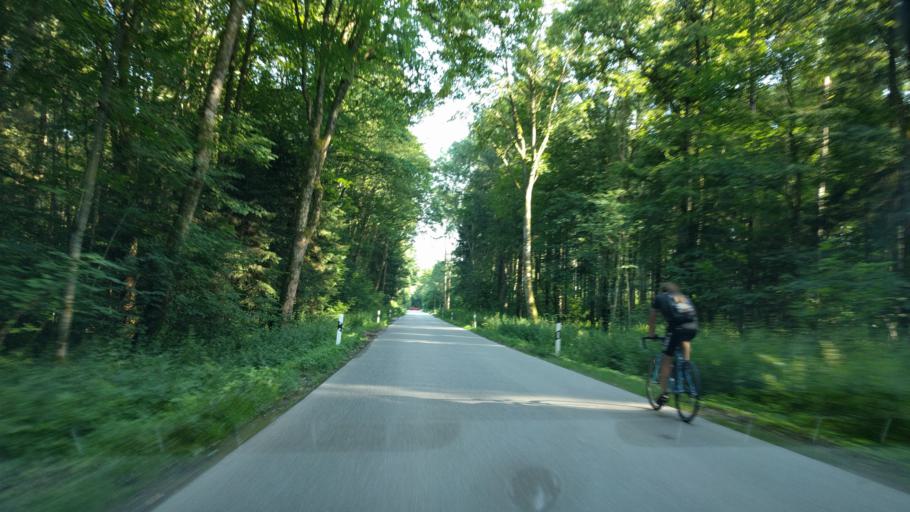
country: DE
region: Bavaria
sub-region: Upper Bavaria
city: Grunwald
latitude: 48.0362
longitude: 11.5502
